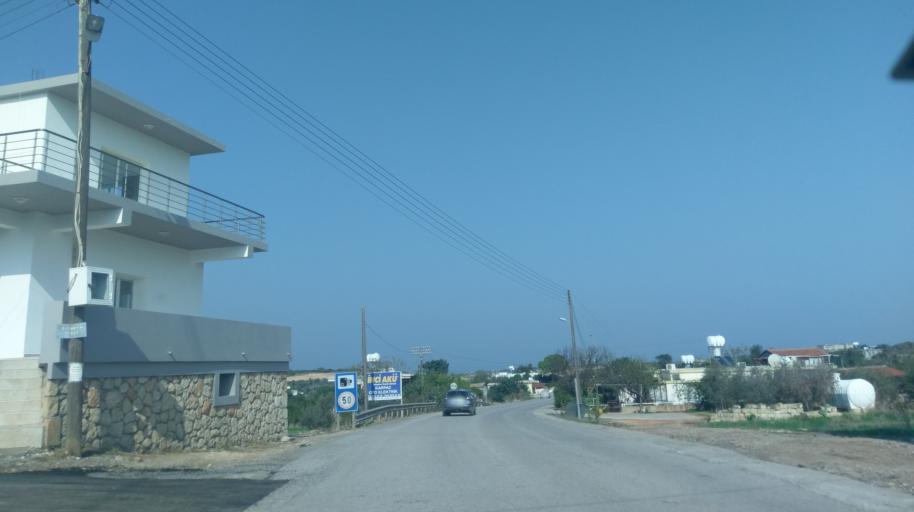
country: CY
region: Ammochostos
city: Leonarisso
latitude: 35.5084
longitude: 34.1605
